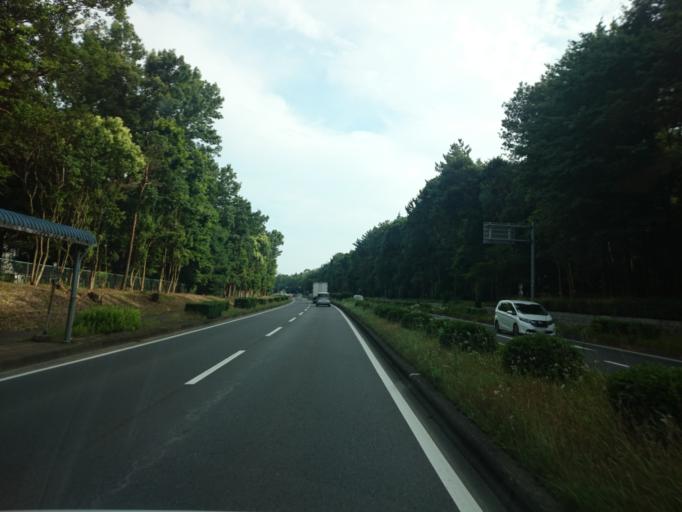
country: JP
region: Ibaraki
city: Tsukuba
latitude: 36.1224
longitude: 140.0738
